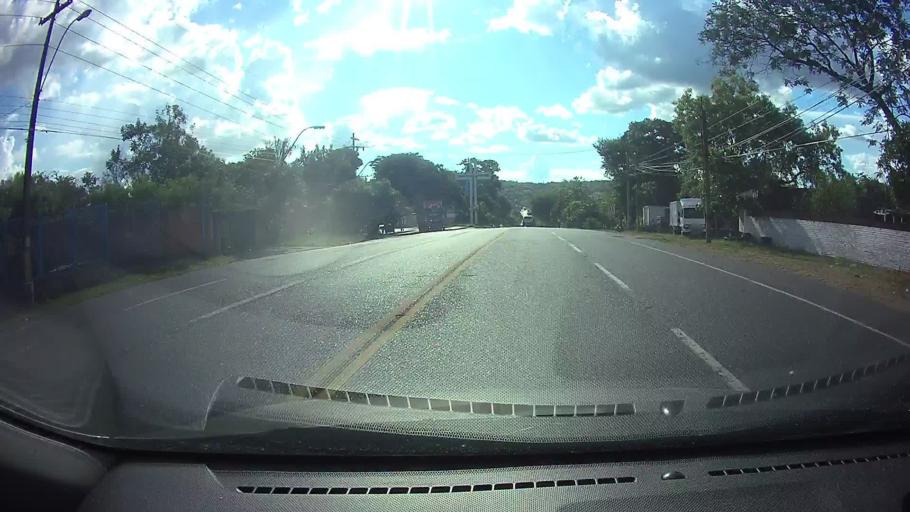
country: PY
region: Cordillera
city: Caacupe
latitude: -25.3840
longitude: -57.1284
